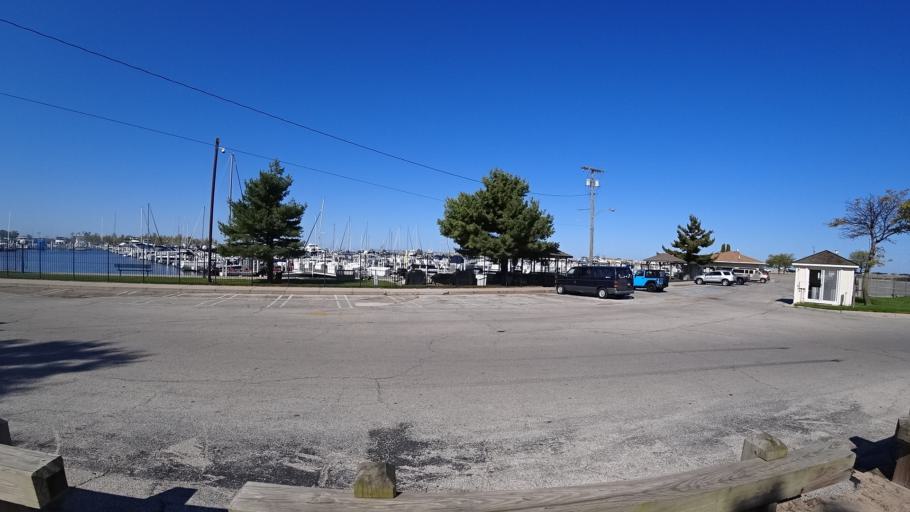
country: US
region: Indiana
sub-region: LaPorte County
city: Michigan City
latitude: 41.7254
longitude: -86.9047
